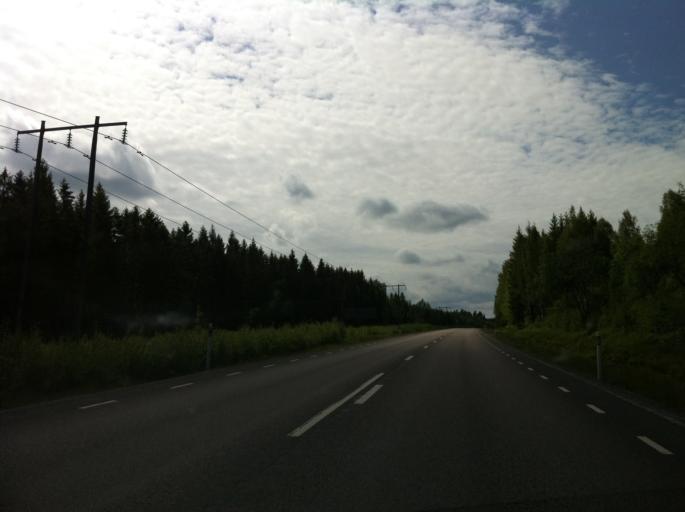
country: SE
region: Vaermland
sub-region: Karlstads Kommun
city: Edsvalla
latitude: 59.4403
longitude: 13.2023
